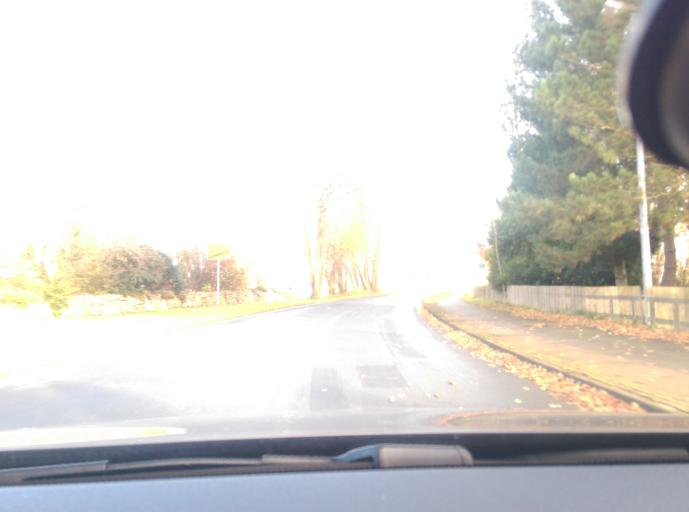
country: DE
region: Lower Saxony
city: Wietze
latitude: 52.6644
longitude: 9.7688
